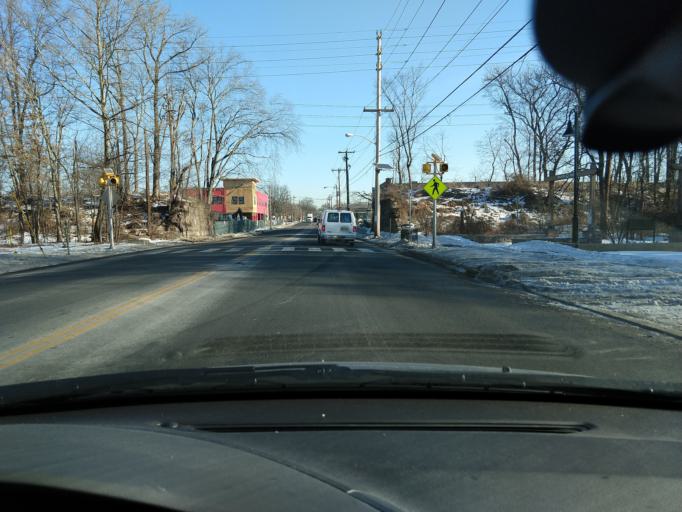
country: US
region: New Jersey
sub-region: Middlesex County
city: Metuchen
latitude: 40.5395
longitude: -74.3685
